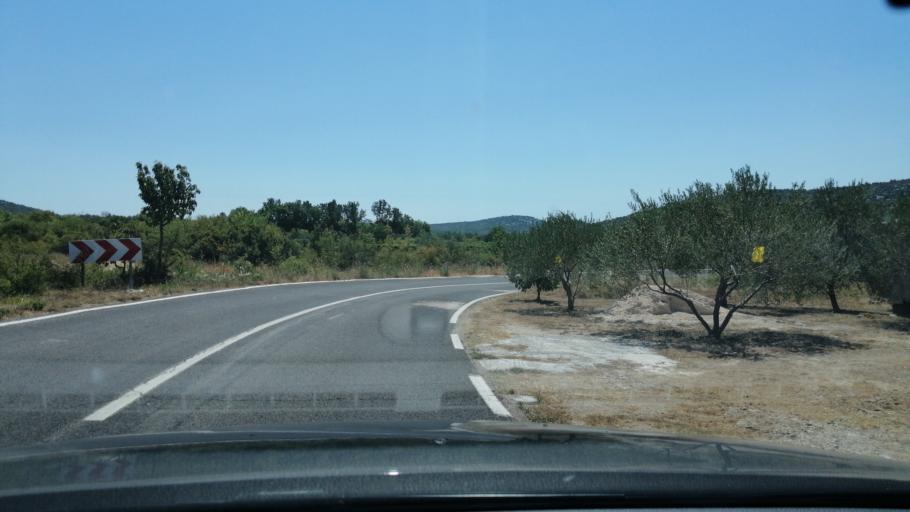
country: HR
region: Sibensko-Kniniska
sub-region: Grad Sibenik
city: Pirovac
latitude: 43.8765
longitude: 15.6815
